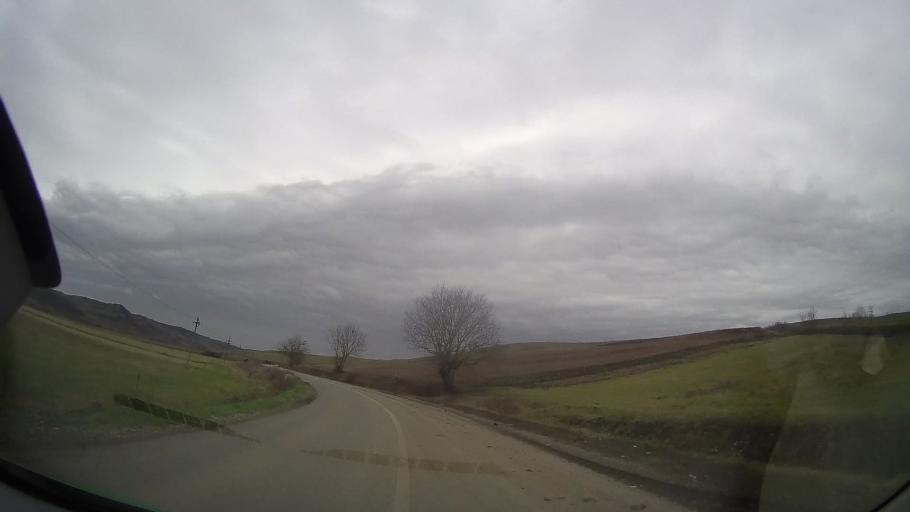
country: RO
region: Bistrita-Nasaud
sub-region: Comuna Milas
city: Milas
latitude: 46.7931
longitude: 24.4210
